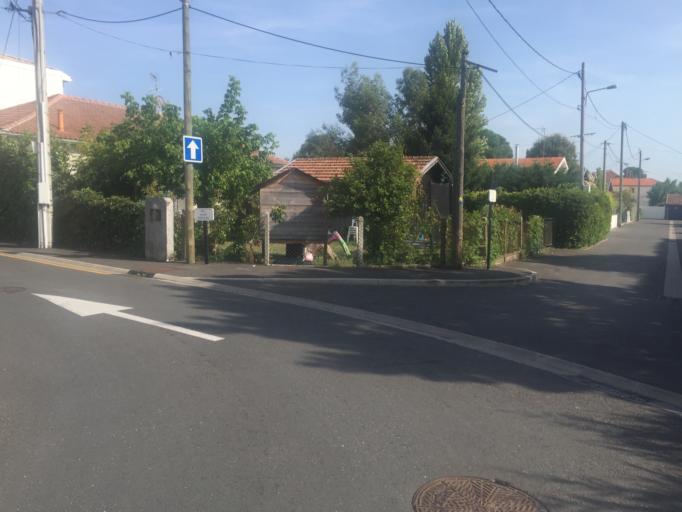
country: FR
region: Aquitaine
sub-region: Departement de la Gironde
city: La Teste-de-Buch
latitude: 44.6368
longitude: -1.1466
